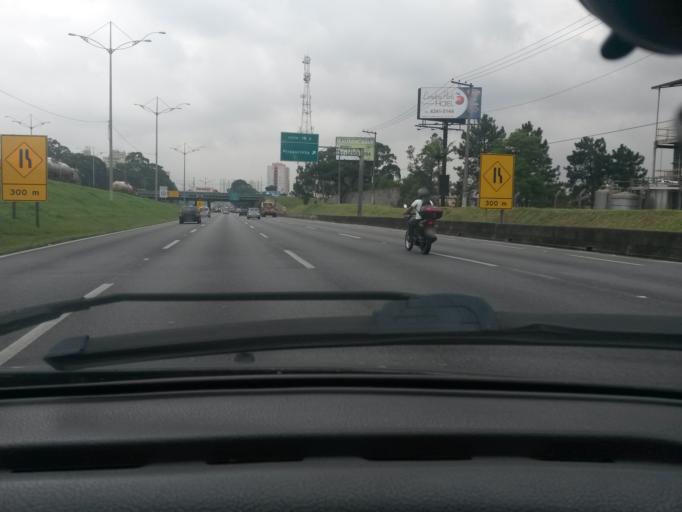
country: BR
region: Sao Paulo
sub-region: Sao Bernardo Do Campo
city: Sao Bernardo do Campo
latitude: -23.6871
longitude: -46.5660
